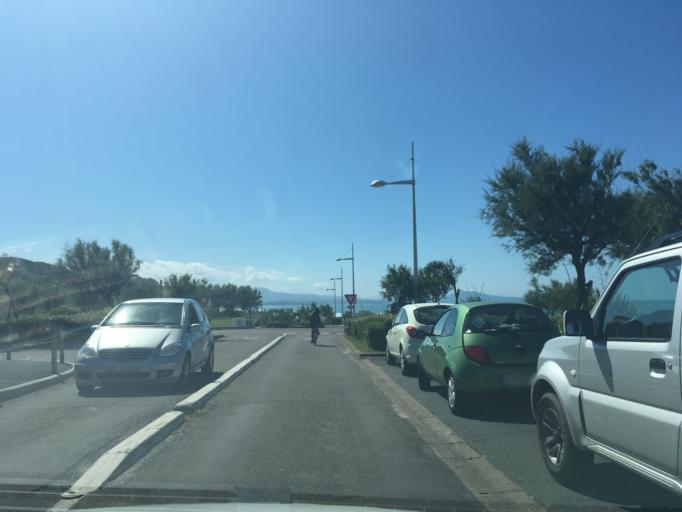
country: FR
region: Aquitaine
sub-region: Departement des Pyrenees-Atlantiques
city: Biarritz
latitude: 43.4629
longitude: -1.5755
